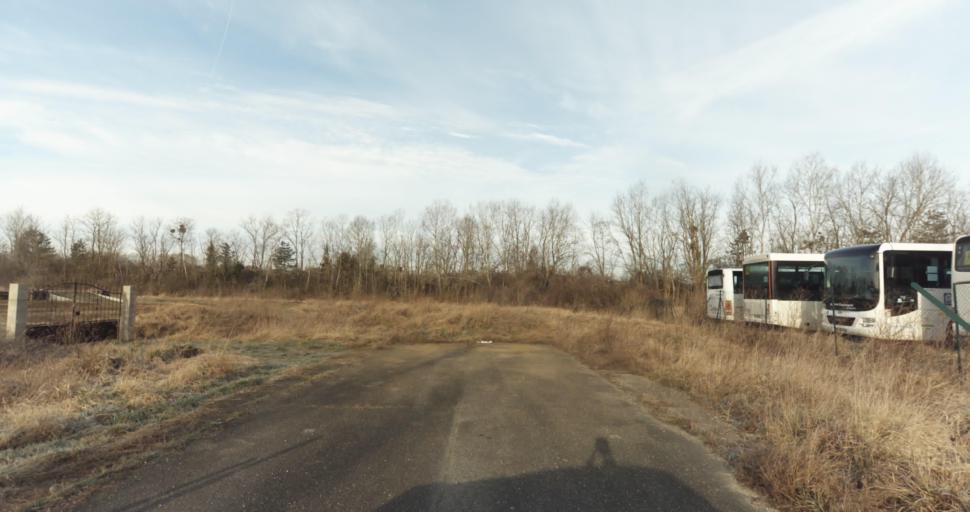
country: FR
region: Lorraine
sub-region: Departement de Meurthe-et-Moselle
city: Jarny
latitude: 49.1557
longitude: 5.8910
